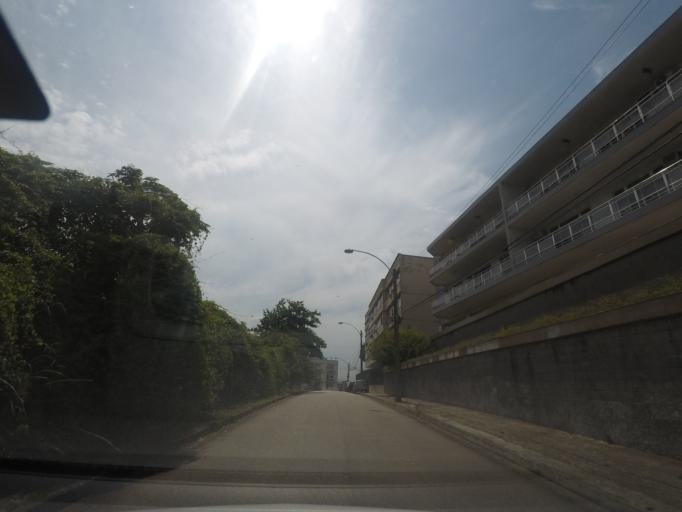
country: BR
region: Rio de Janeiro
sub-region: Rio De Janeiro
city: Rio de Janeiro
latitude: -22.8148
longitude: -43.2093
